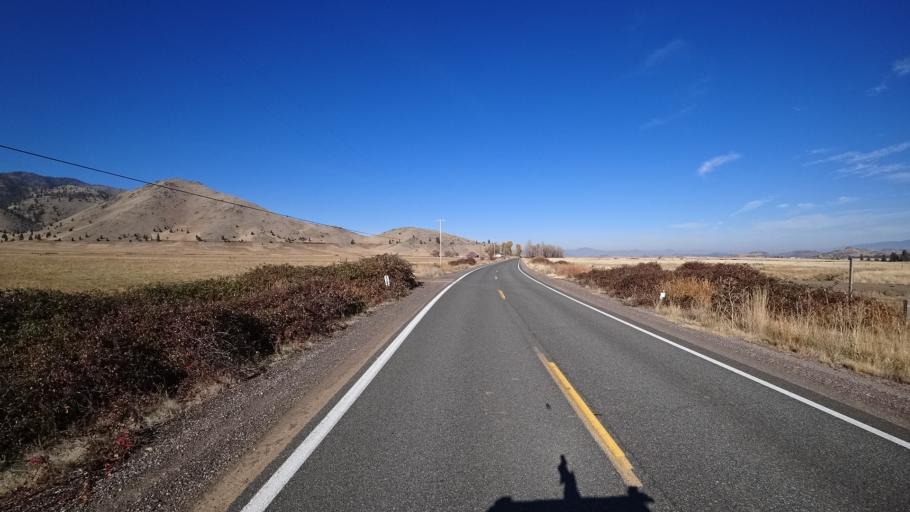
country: US
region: California
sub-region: Siskiyou County
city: Weed
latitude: 41.4545
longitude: -122.4589
